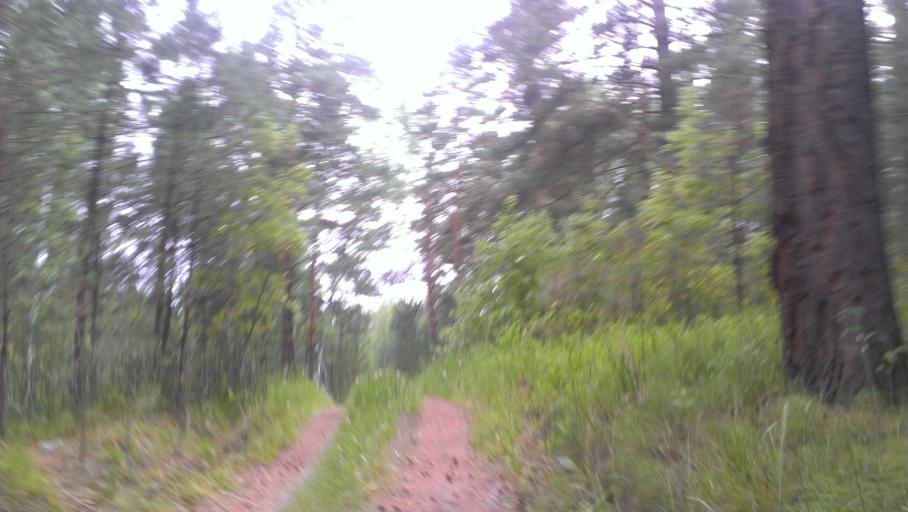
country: RU
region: Altai Krai
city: Sannikovo
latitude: 53.3491
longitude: 84.0380
